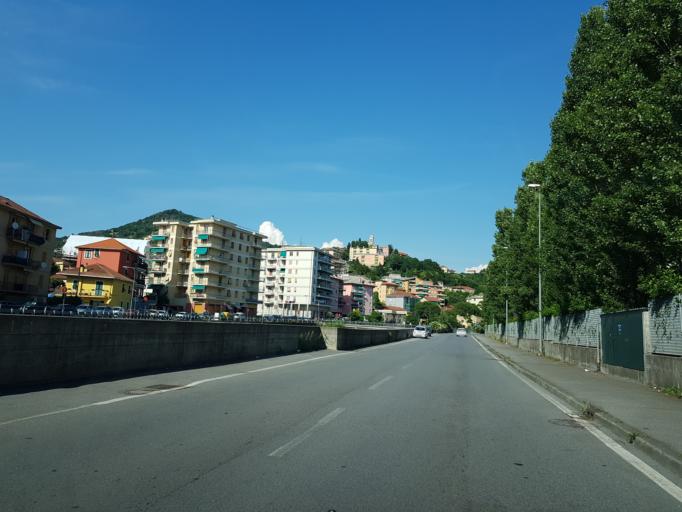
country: IT
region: Liguria
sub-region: Provincia di Genova
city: Manesseno
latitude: 44.4765
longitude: 8.9198
